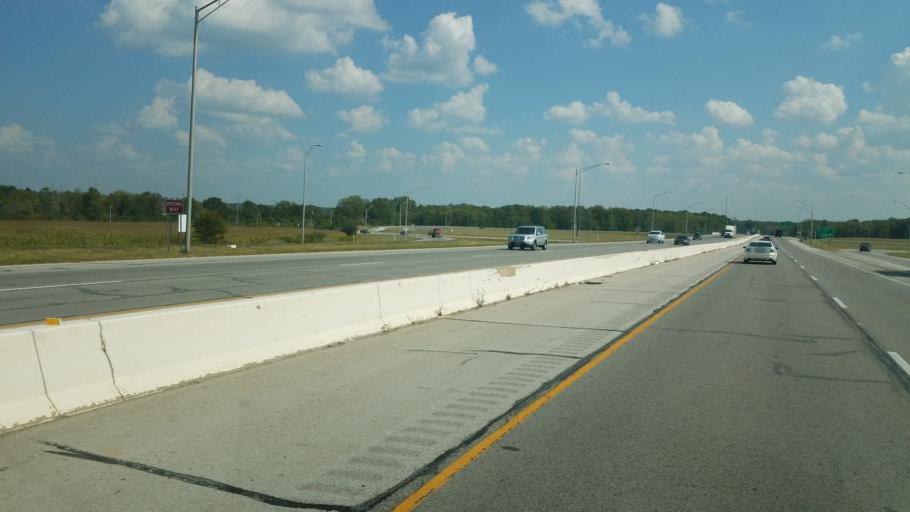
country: US
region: Indiana
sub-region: Allen County
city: Fort Wayne
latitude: 41.1612
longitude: -85.0683
